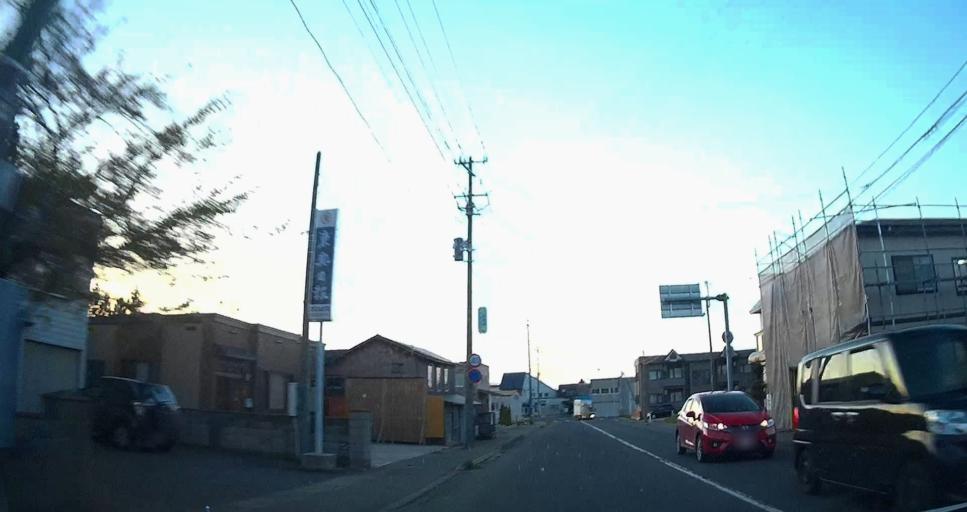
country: JP
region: Aomori
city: Misawa
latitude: 40.8675
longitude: 141.1228
